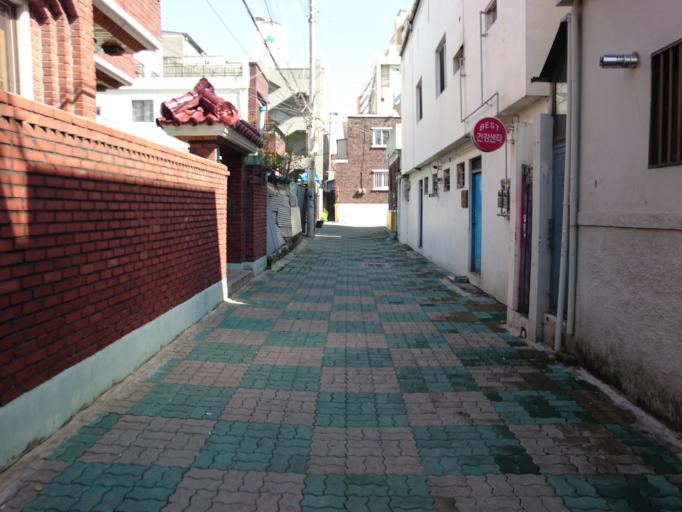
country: KR
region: Daegu
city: Daegu
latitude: 35.8551
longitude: 128.6524
